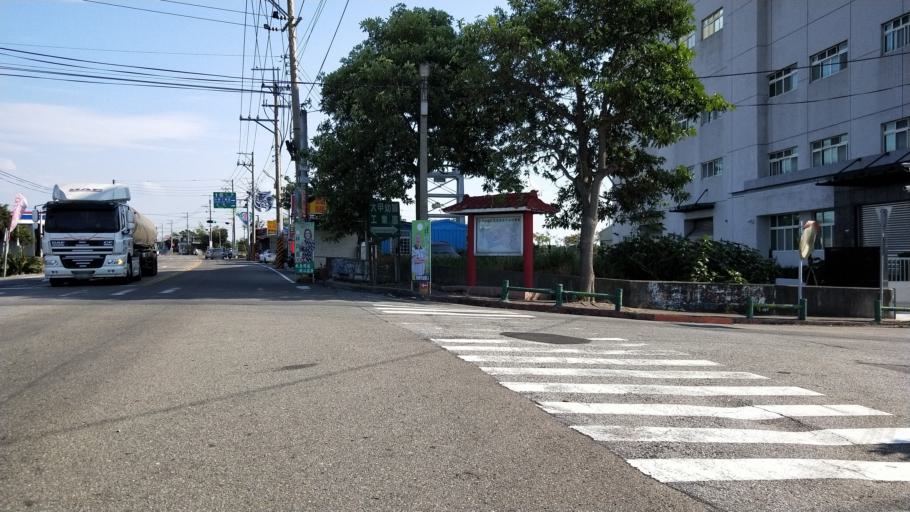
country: TW
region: Taiwan
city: Fengyuan
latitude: 24.4023
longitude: 120.6638
